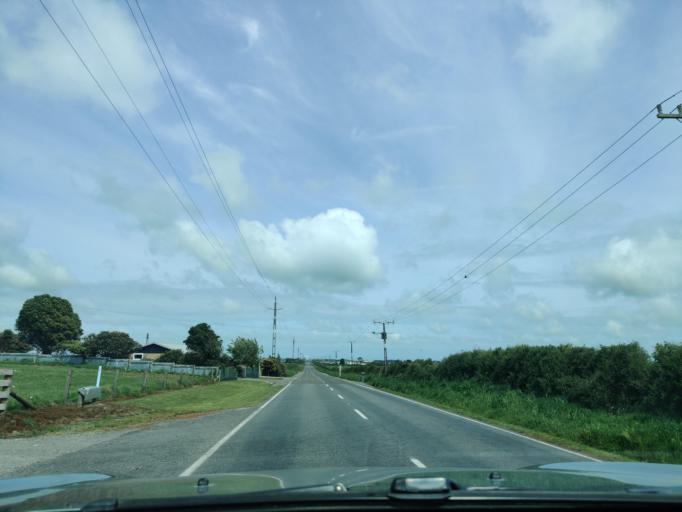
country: NZ
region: Taranaki
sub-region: South Taranaki District
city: Eltham
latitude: -39.4282
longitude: 174.1697
